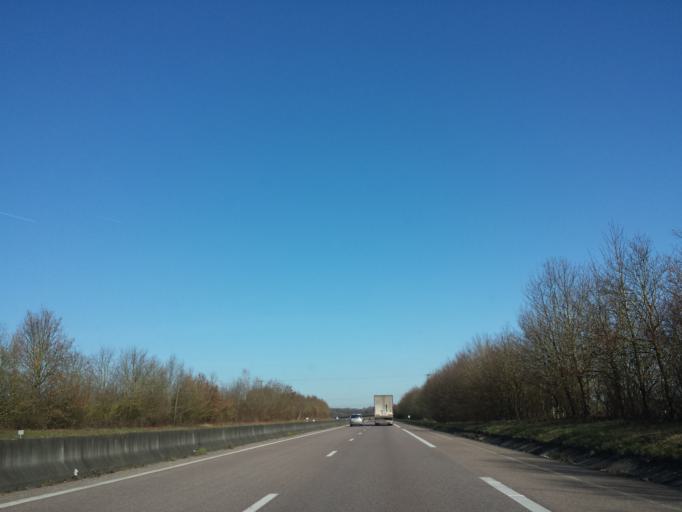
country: FR
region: Picardie
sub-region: Departement de l'Oise
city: Lormaison
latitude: 49.2588
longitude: 2.0935
